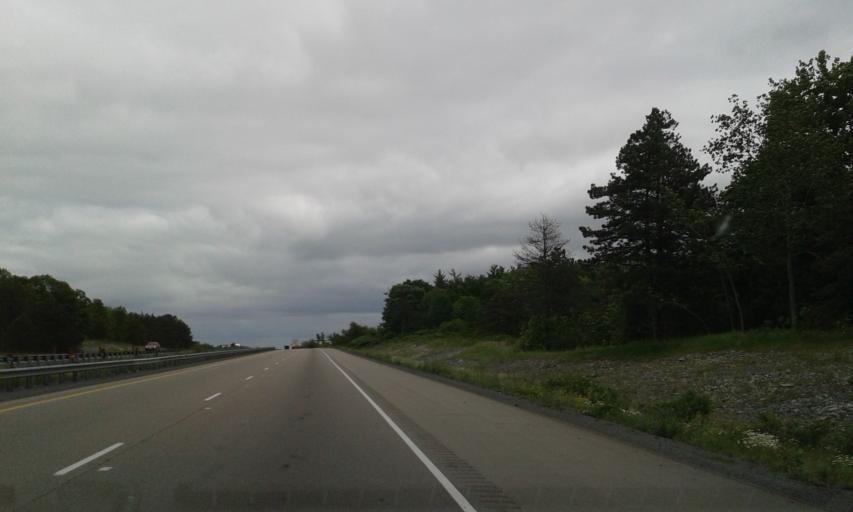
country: CA
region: Ontario
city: Skatepark
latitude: 44.2826
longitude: -76.7109
